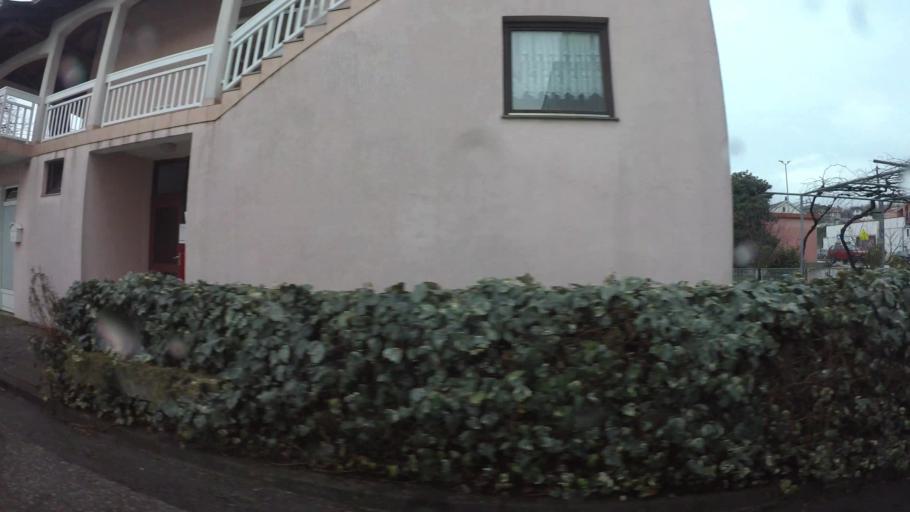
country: BA
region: Federation of Bosnia and Herzegovina
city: Cim
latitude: 43.3512
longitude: 17.7921
